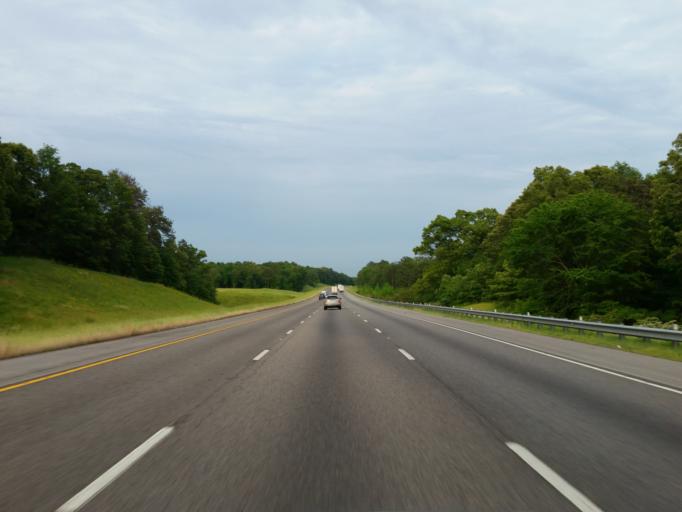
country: US
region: Alabama
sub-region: Calhoun County
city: Bynum
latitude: 33.5778
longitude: -85.9780
